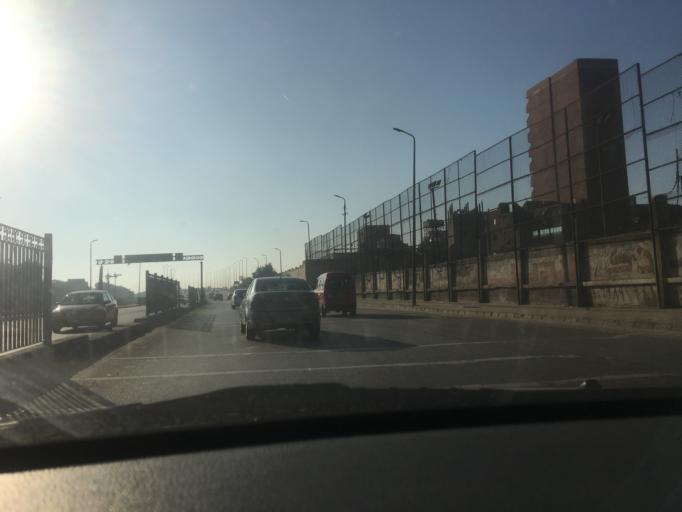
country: EG
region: Muhafazat al Qahirah
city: Cairo
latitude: 30.0130
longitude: 31.2669
